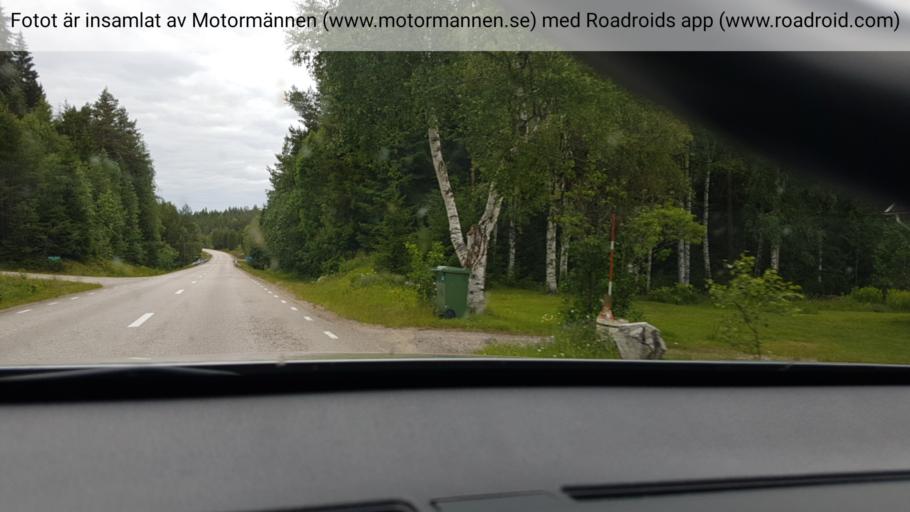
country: NO
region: Hedmark
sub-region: Trysil
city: Innbygda
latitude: 60.9275
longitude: 12.5125
